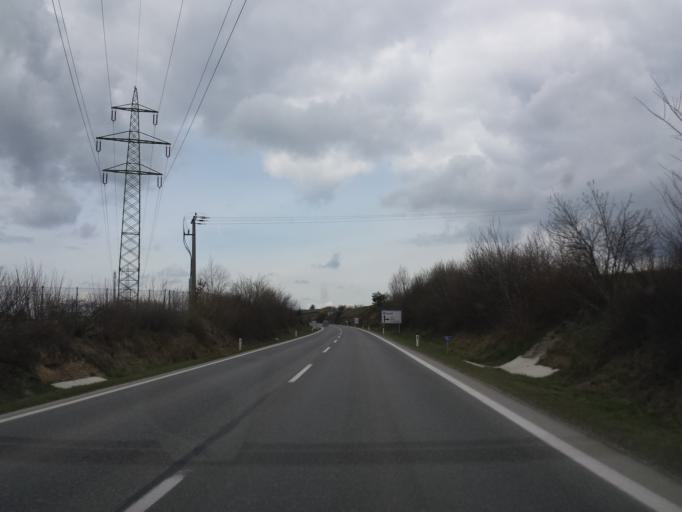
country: AT
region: Lower Austria
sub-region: Politischer Bezirk Krems
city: Gfohl
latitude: 48.5206
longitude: 15.5019
